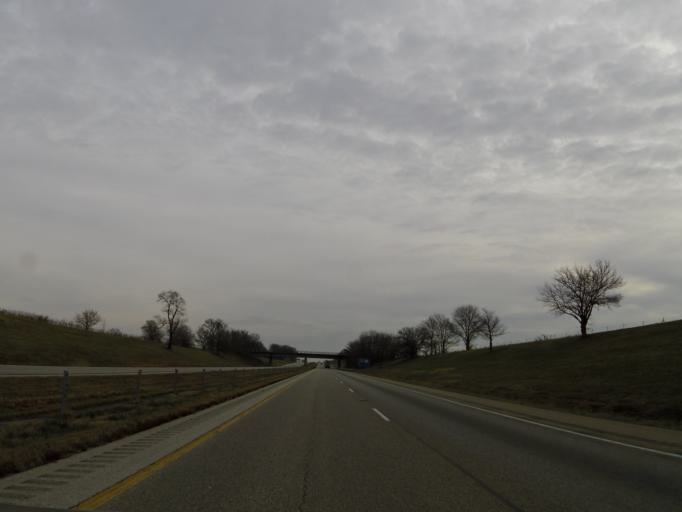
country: US
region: Illinois
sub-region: Vermilion County
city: Danville
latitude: 40.1153
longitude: -87.5624
